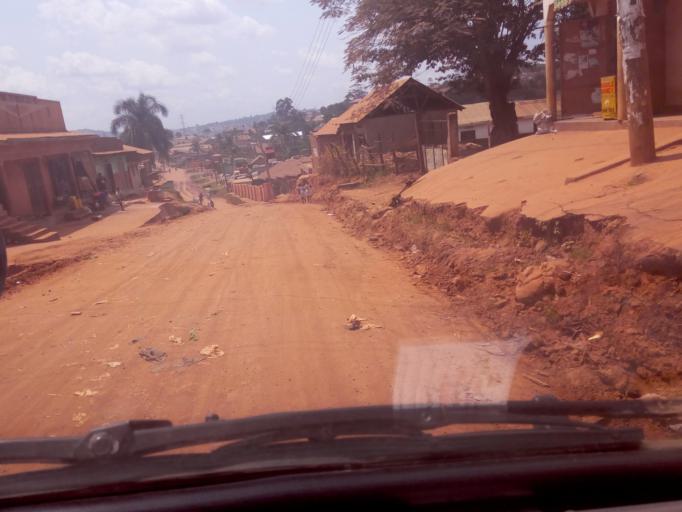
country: UG
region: Central Region
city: Kampala Central Division
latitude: 0.3440
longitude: 32.5555
